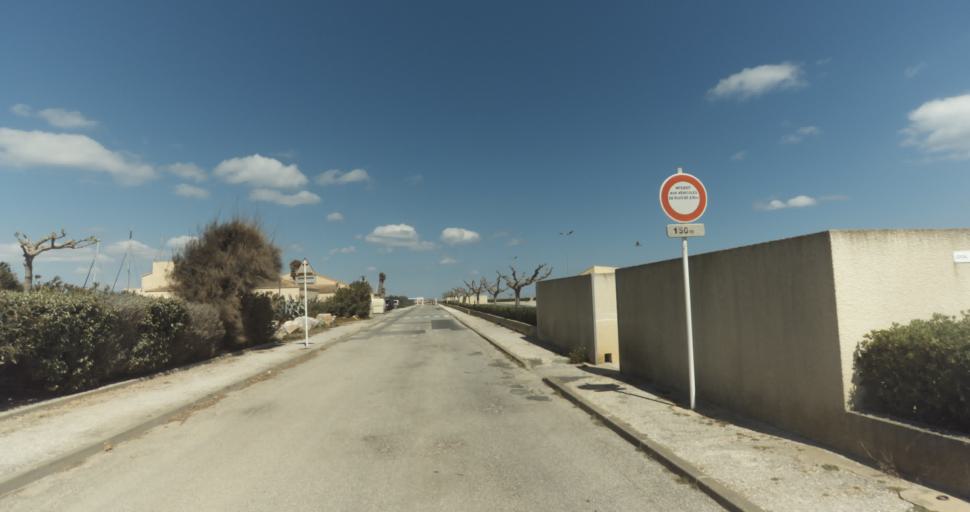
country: FR
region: Languedoc-Roussillon
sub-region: Departement de l'Aude
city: Leucate
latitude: 42.8688
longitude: 3.0453
